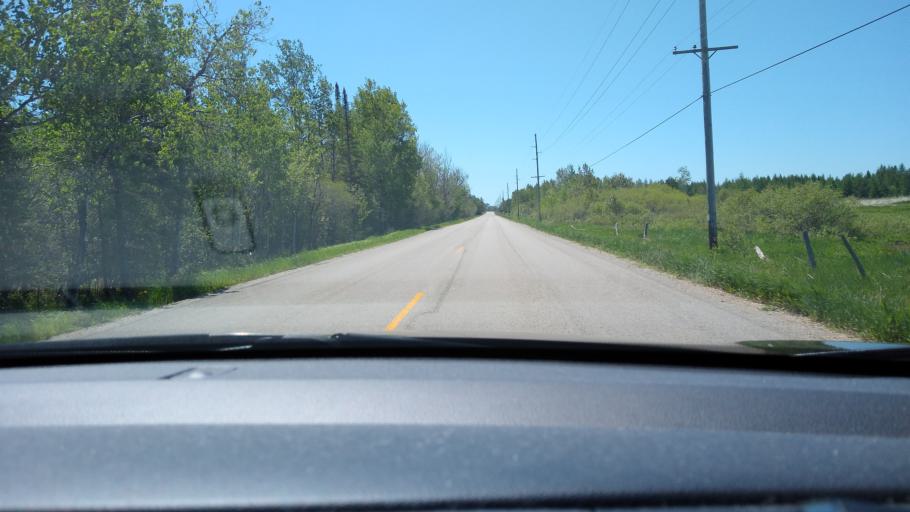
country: US
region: Michigan
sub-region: Delta County
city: Gladstone
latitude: 45.8574
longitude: -87.1841
